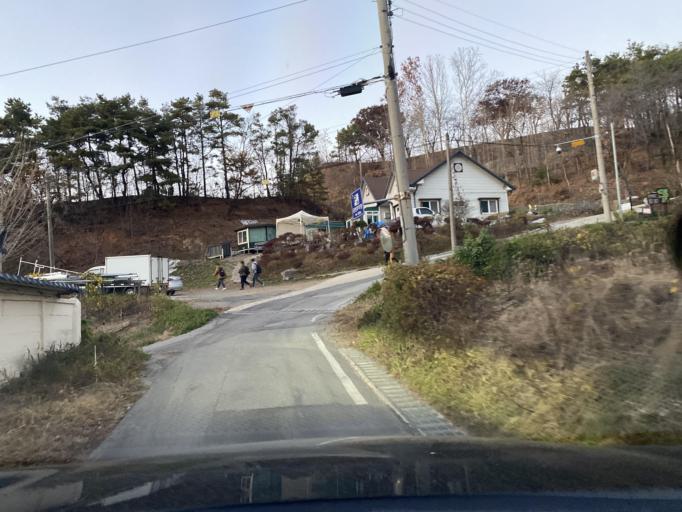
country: KR
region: Chungcheongnam-do
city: Yesan
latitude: 36.6831
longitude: 126.8375
